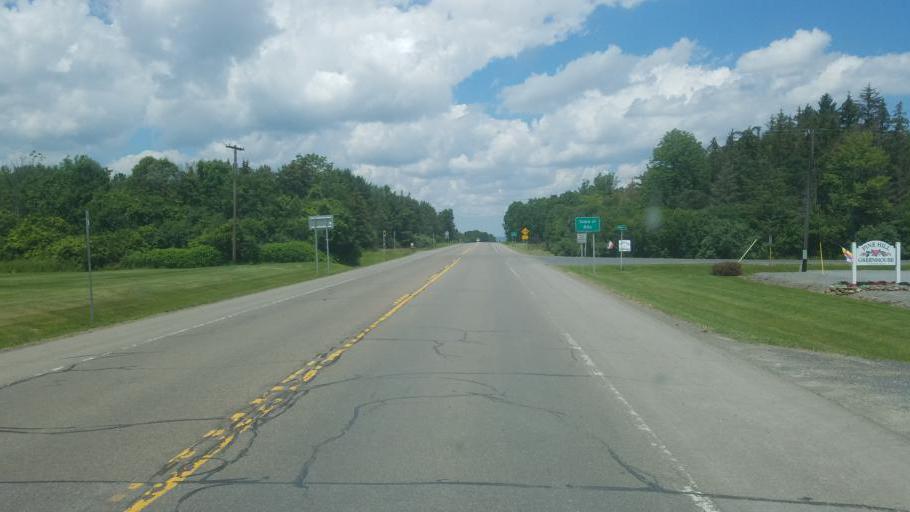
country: US
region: New York
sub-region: Yates County
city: Keuka Park
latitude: 42.5778
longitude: -77.0361
